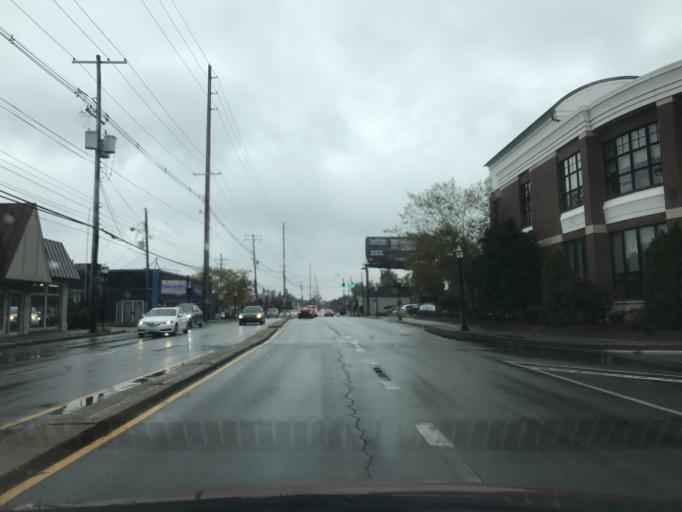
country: US
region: Kentucky
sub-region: Jefferson County
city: Saint Matthews
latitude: 38.2530
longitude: -85.6557
